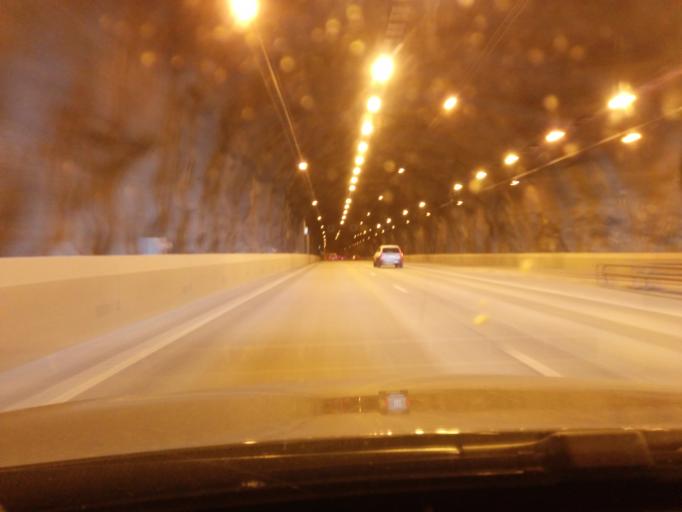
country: SE
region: Stockholm
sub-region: Sollentuna Kommun
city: Sollentuna
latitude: 59.4483
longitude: 17.9442
